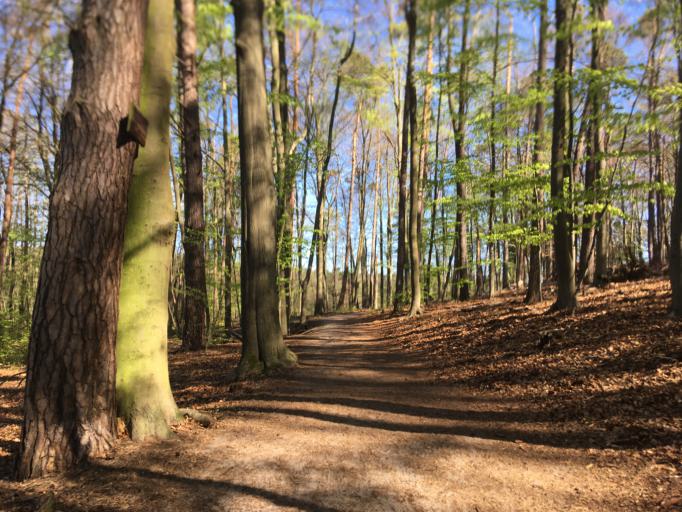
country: DE
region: Brandenburg
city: Wandlitz
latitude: 52.7527
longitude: 13.5297
